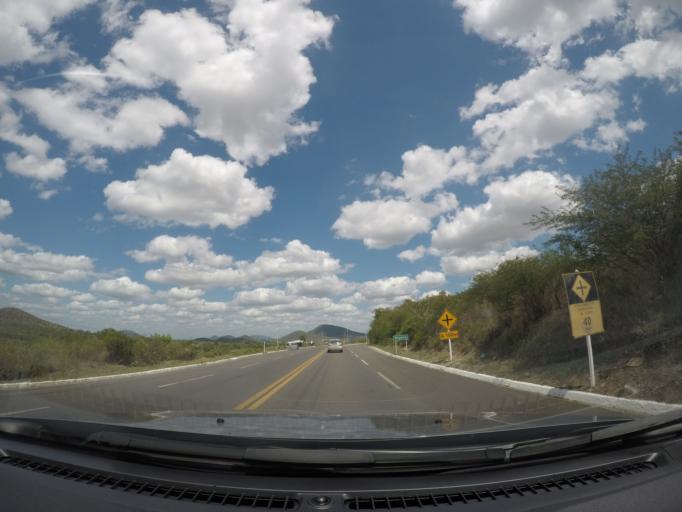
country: BR
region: Bahia
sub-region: Anguera
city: Anguera
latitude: -12.1654
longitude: -39.2413
